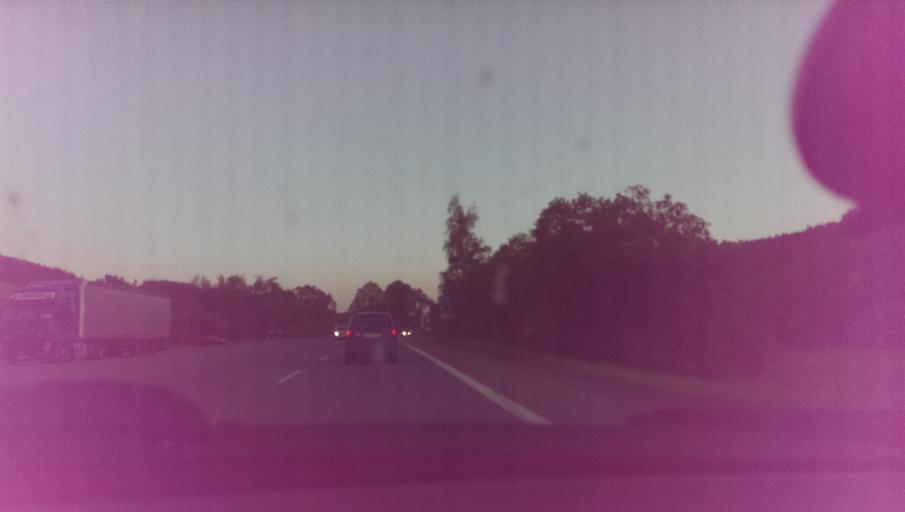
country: CZ
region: Zlin
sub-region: Okres Vsetin
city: Vsetin
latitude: 49.3126
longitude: 18.0047
